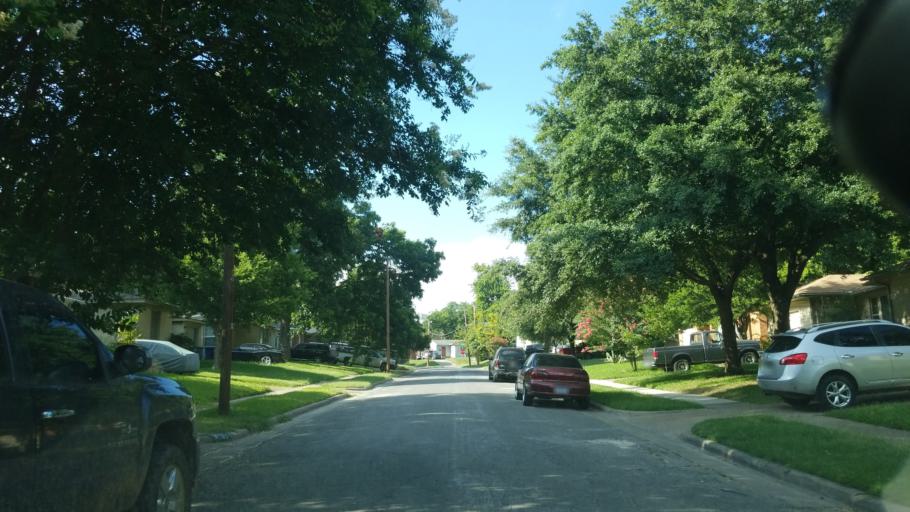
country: US
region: Texas
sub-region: Dallas County
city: Balch Springs
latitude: 32.7652
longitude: -96.7061
